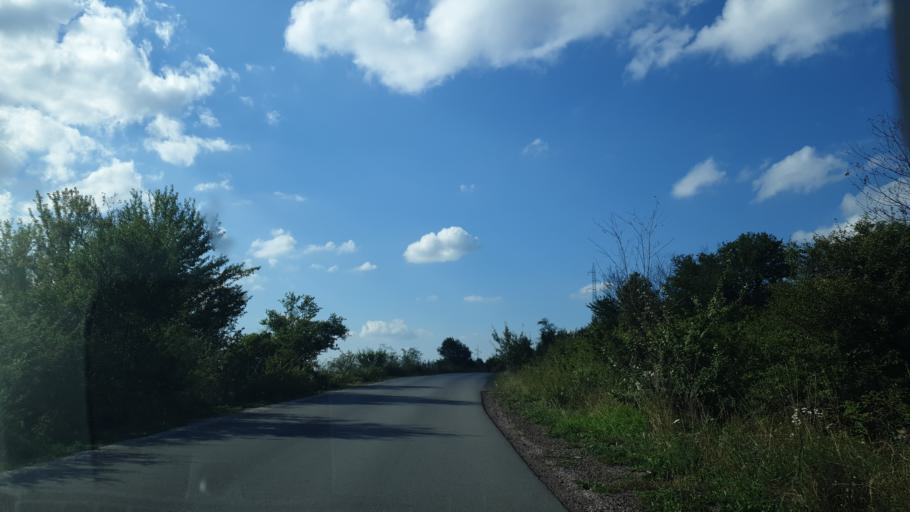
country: RS
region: Central Serbia
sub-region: Zlatiborski Okrug
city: Nova Varos
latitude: 43.4274
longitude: 19.8969
